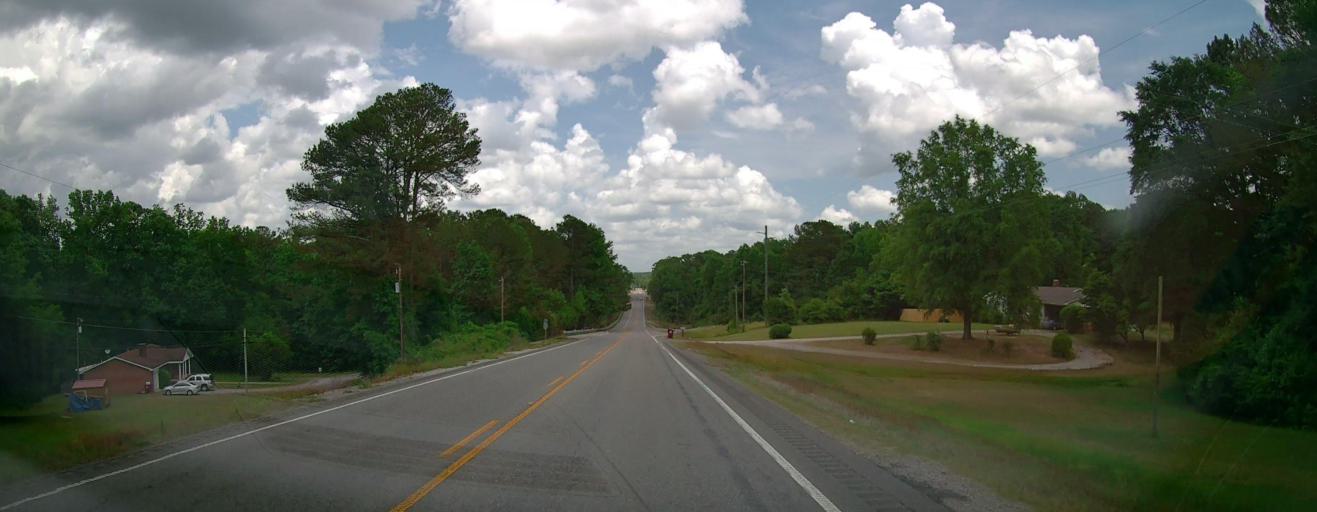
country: US
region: Alabama
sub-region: Marion County
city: Hamilton
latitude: 34.1375
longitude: -88.0033
